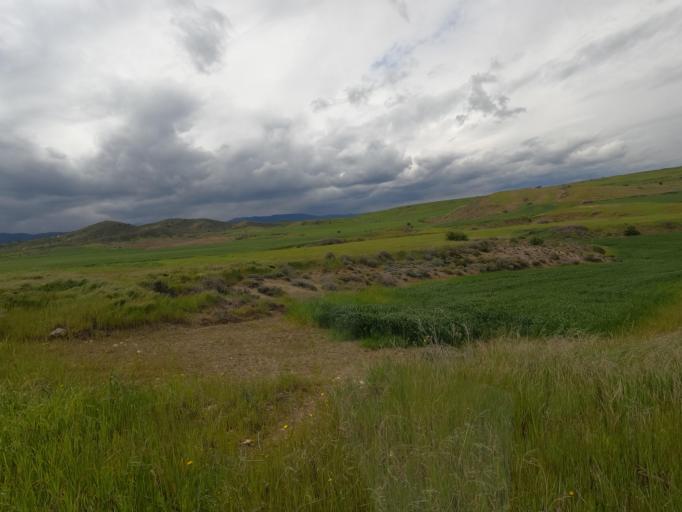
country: CY
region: Lefkosia
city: Lefka
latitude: 35.0961
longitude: 32.9424
